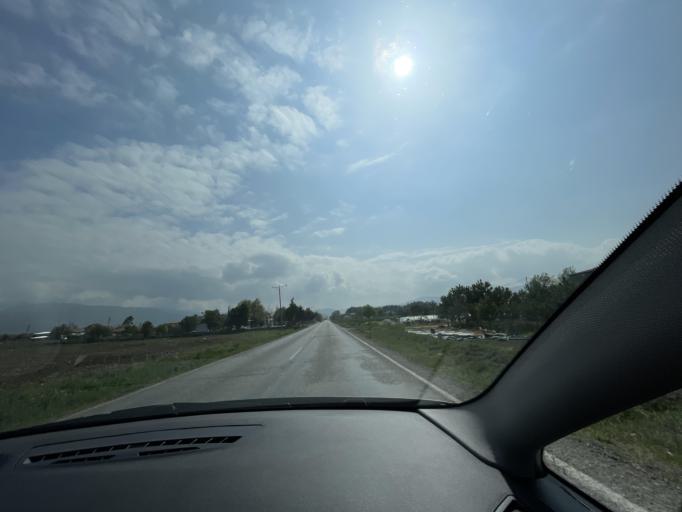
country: TR
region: Denizli
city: Acipayam
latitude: 37.5077
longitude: 29.3974
